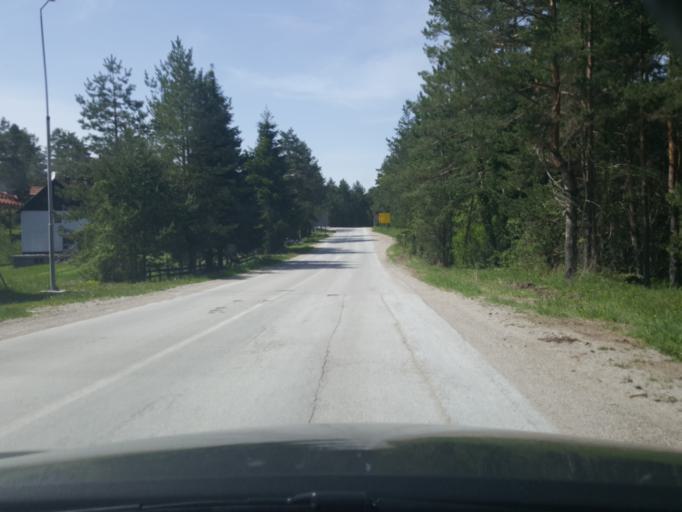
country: RS
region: Central Serbia
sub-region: Zlatiborski Okrug
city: Bajina Basta
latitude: 43.8870
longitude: 19.5423
